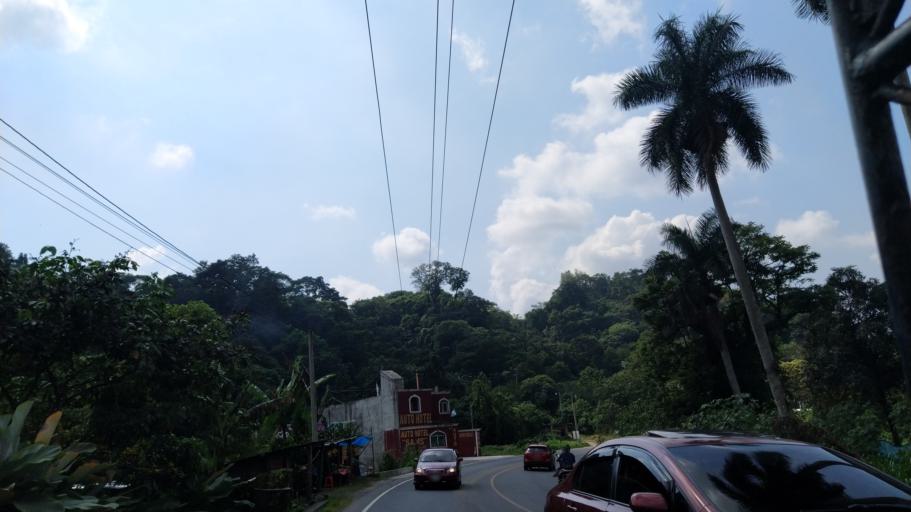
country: GT
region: Quetzaltenango
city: El Palmar
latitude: 14.6491
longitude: -91.5648
